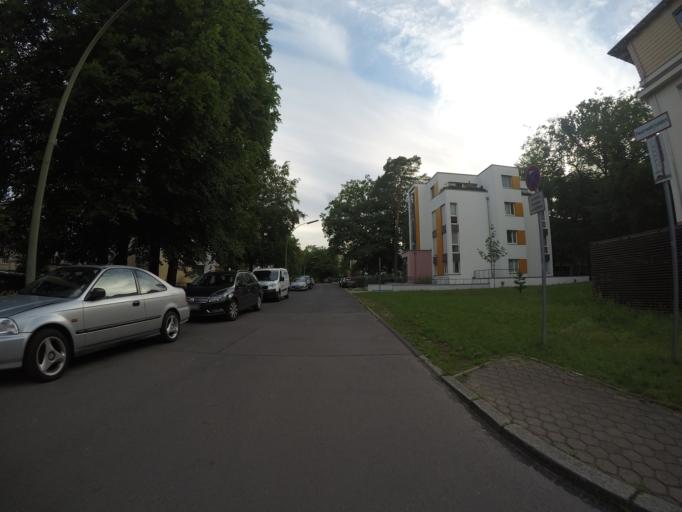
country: DE
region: Berlin
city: Dahlem
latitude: 52.4568
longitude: 13.2704
